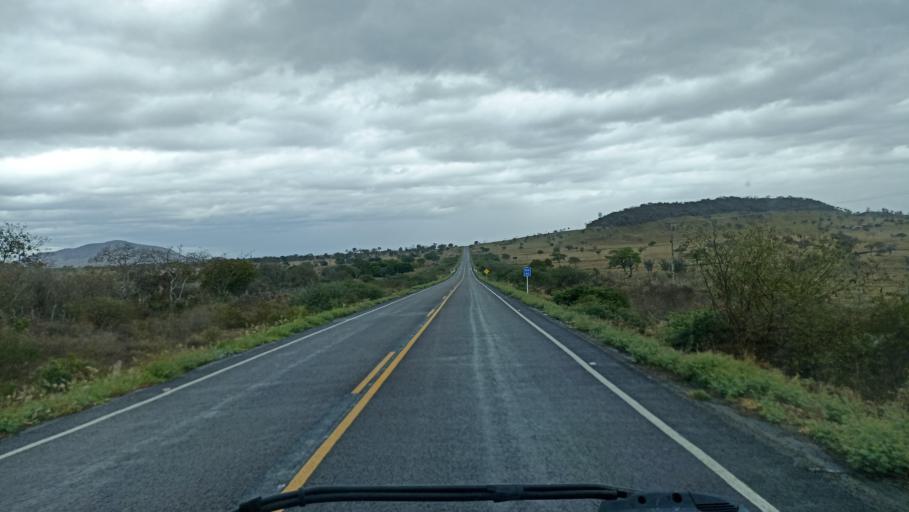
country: BR
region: Bahia
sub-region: Iacu
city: Iacu
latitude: -12.9619
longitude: -40.4807
